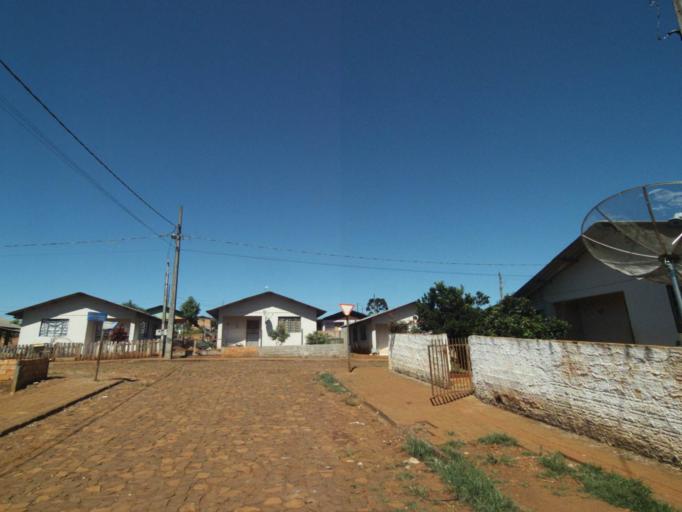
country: BR
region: Santa Catarina
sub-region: Sao Lourenco Do Oeste
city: Sao Lourenco dOeste
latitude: -26.2724
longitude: -52.7767
